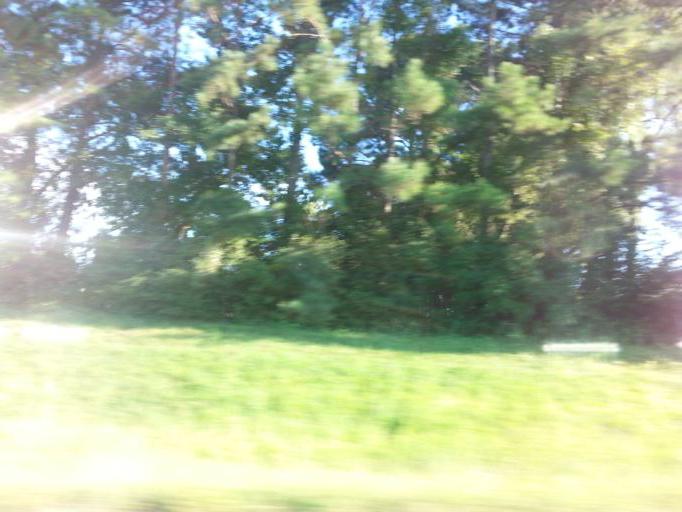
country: US
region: Alabama
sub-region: Lauderdale County
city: Killen
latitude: 34.8562
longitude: -87.5506
